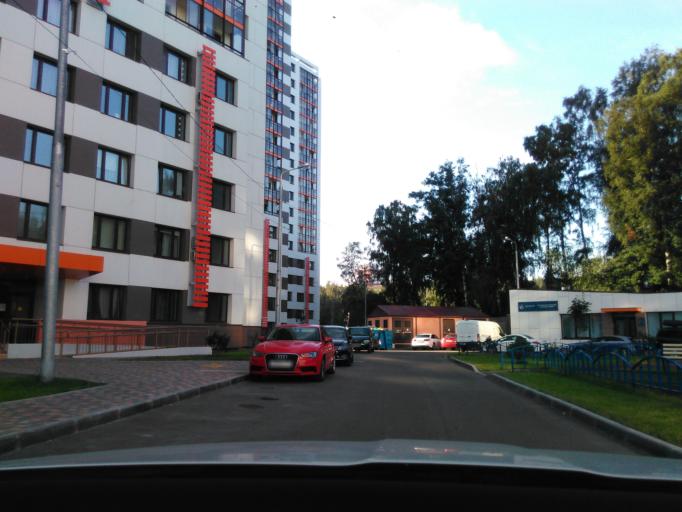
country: RU
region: Moscow
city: Khimki
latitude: 55.8963
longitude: 37.4215
